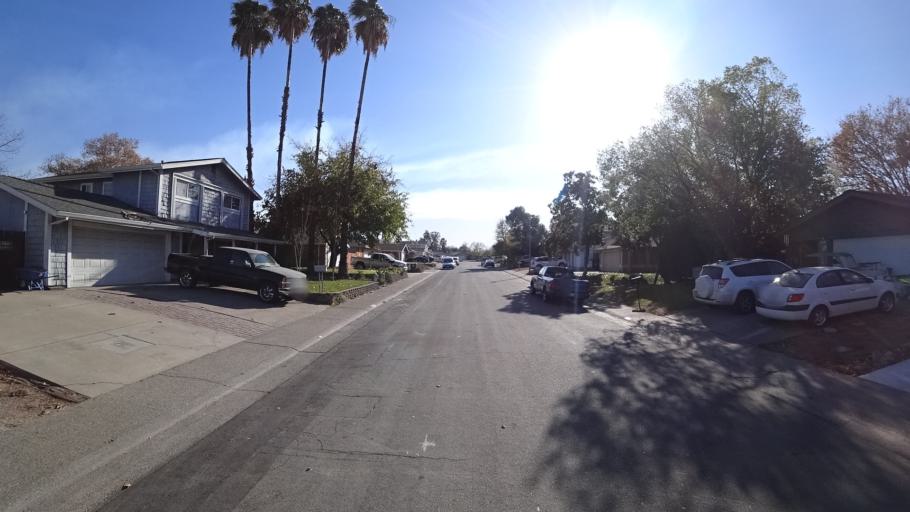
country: US
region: California
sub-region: Sacramento County
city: Antelope
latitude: 38.6987
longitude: -121.3243
